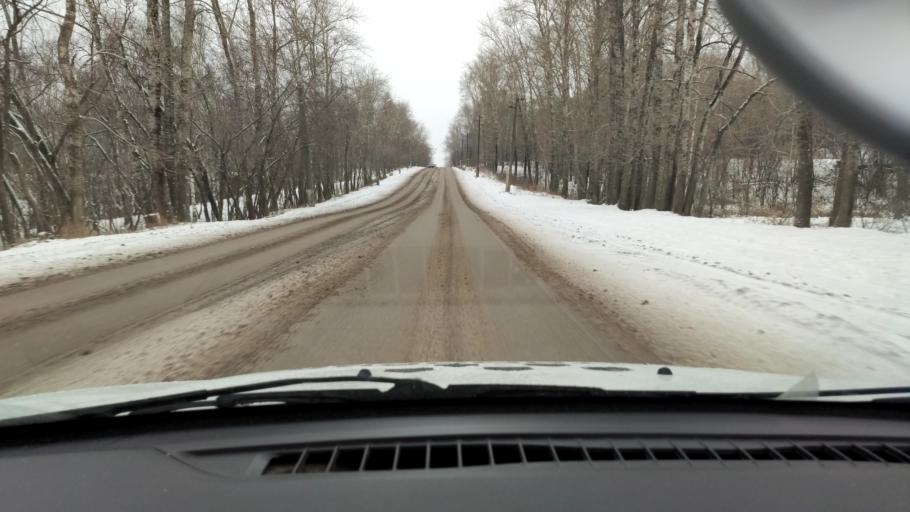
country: RU
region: Perm
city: Perm
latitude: 58.1239
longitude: 56.3706
